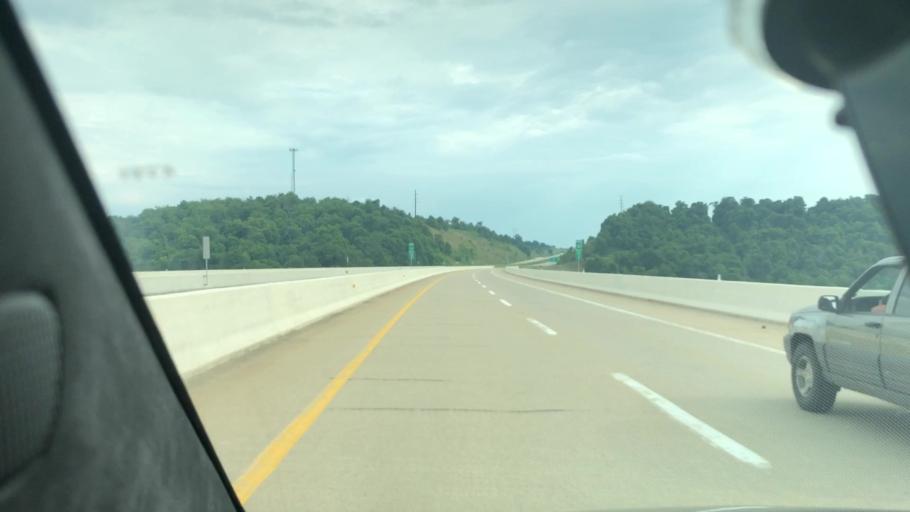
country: US
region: Pennsylvania
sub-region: Washington County
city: Baidland
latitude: 40.2104
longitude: -79.9849
